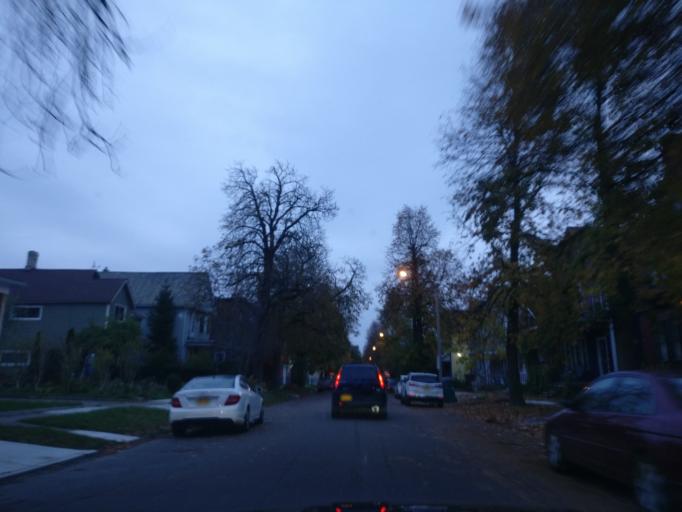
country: US
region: New York
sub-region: Erie County
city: Buffalo
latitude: 42.9024
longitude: -78.8880
